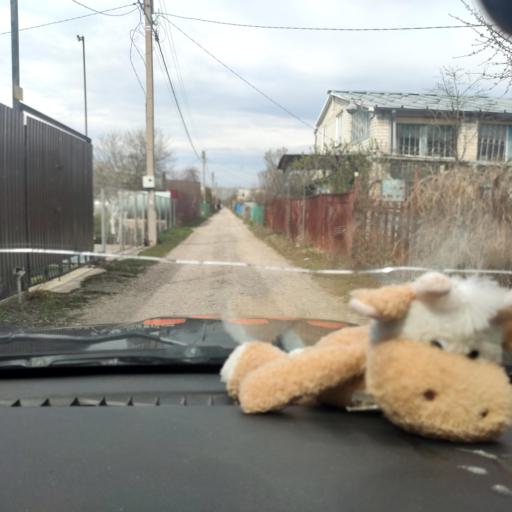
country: RU
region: Samara
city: Tol'yatti
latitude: 53.5995
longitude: 49.2403
